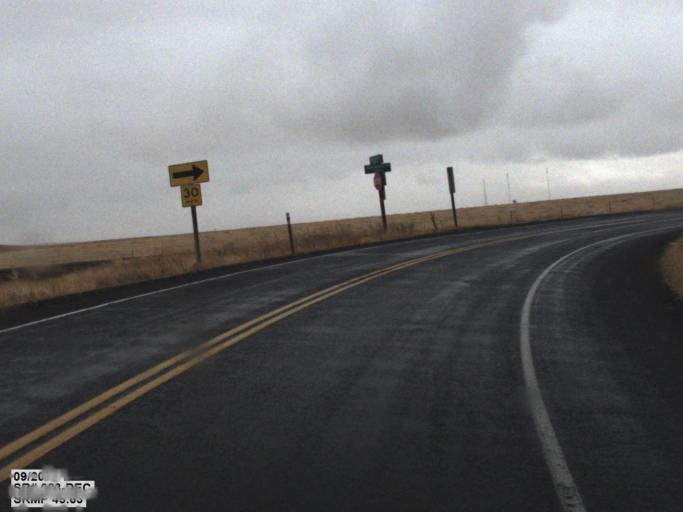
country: US
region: Washington
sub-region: Lincoln County
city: Davenport
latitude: 47.3338
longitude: -117.9836
